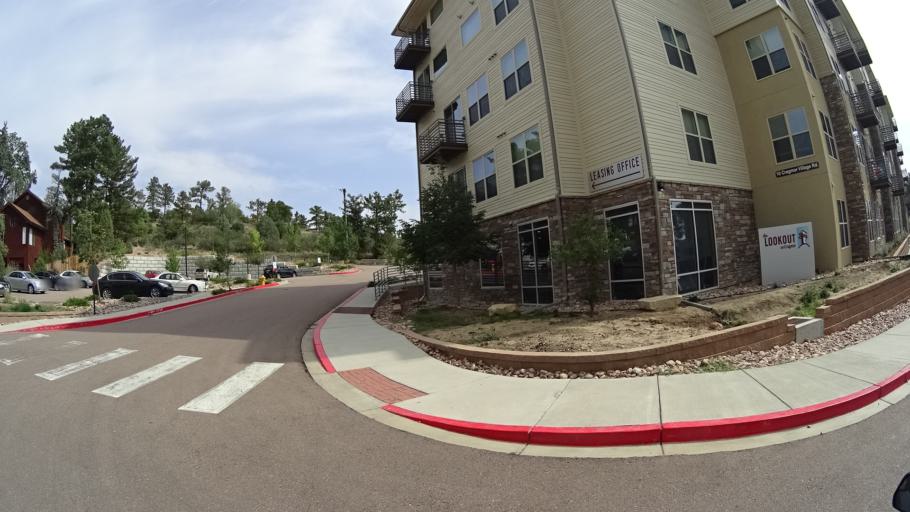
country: US
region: Colorado
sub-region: El Paso County
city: Colorado Springs
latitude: 38.8900
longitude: -104.7938
